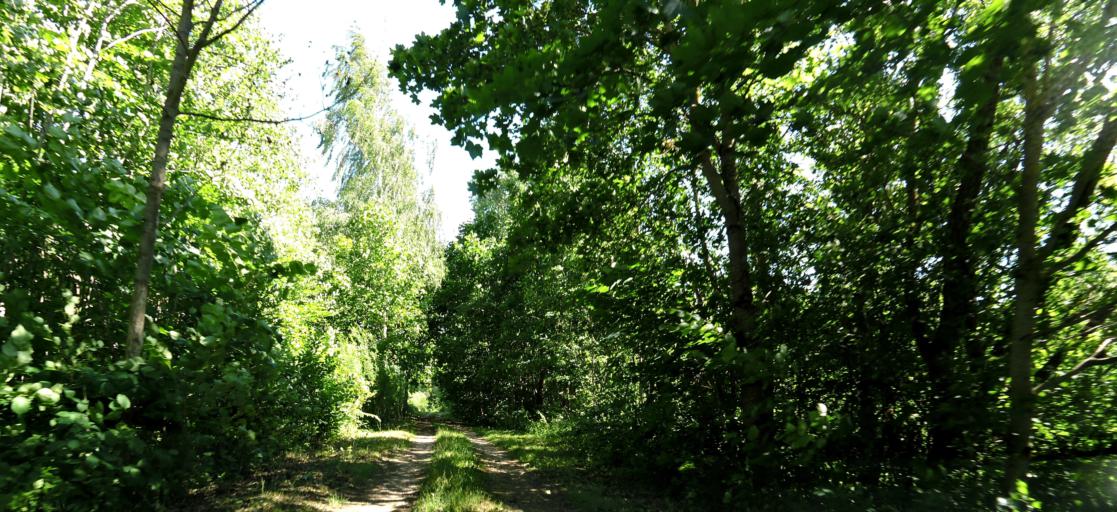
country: LT
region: Panevezys
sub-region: Birzai
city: Birzai
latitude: 56.3839
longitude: 24.7013
